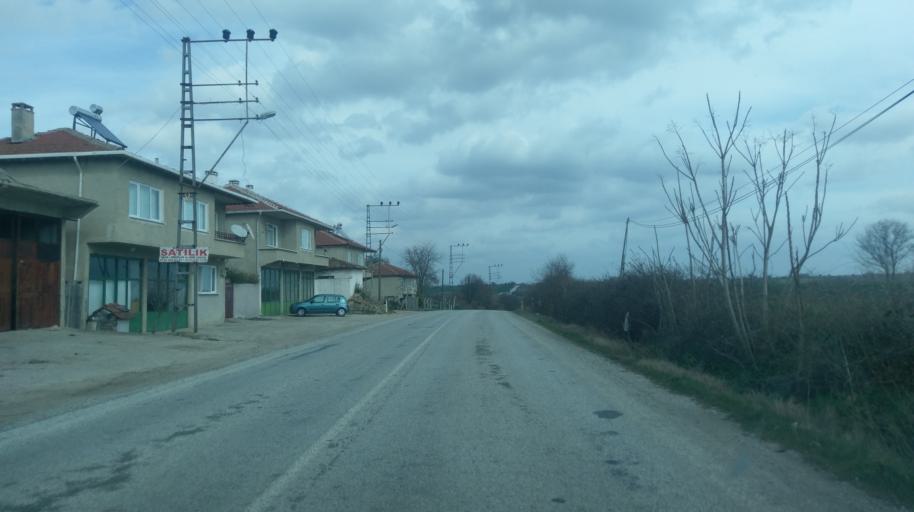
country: TR
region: Kirklareli
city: Inece
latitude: 41.6709
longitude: 26.9847
